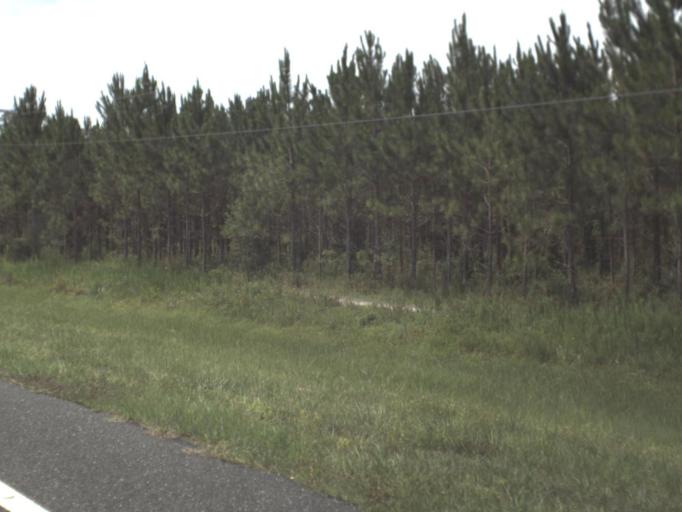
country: US
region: Florida
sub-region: Levy County
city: Chiefland
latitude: 29.4112
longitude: -82.8200
